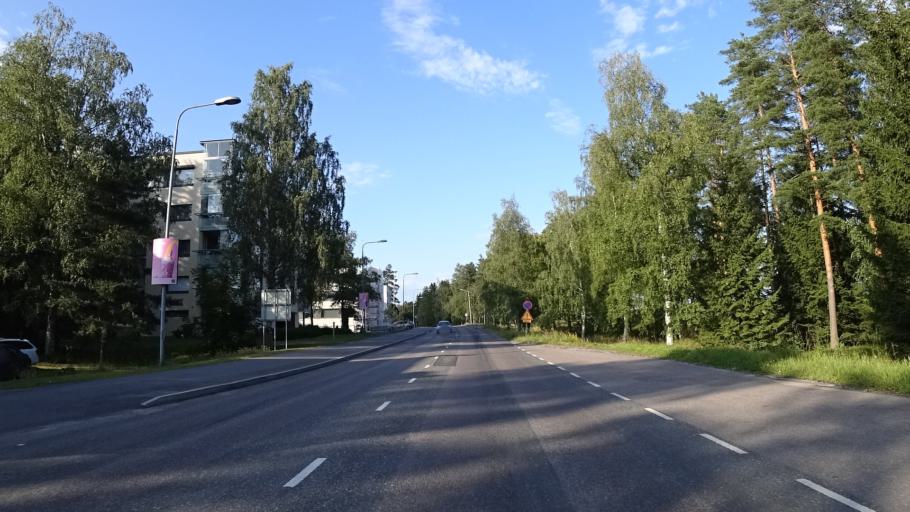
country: FI
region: South Karelia
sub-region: Imatra
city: Imatra
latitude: 61.1727
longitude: 28.7755
